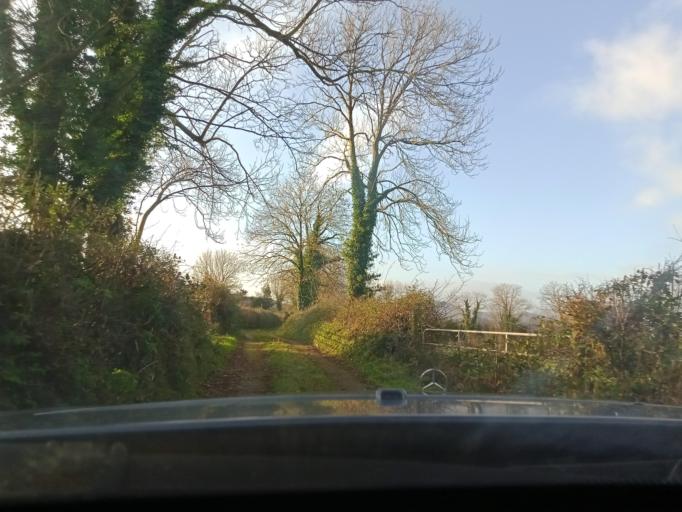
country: IE
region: Leinster
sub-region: Kilkenny
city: Callan
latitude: 52.4826
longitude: -7.4341
